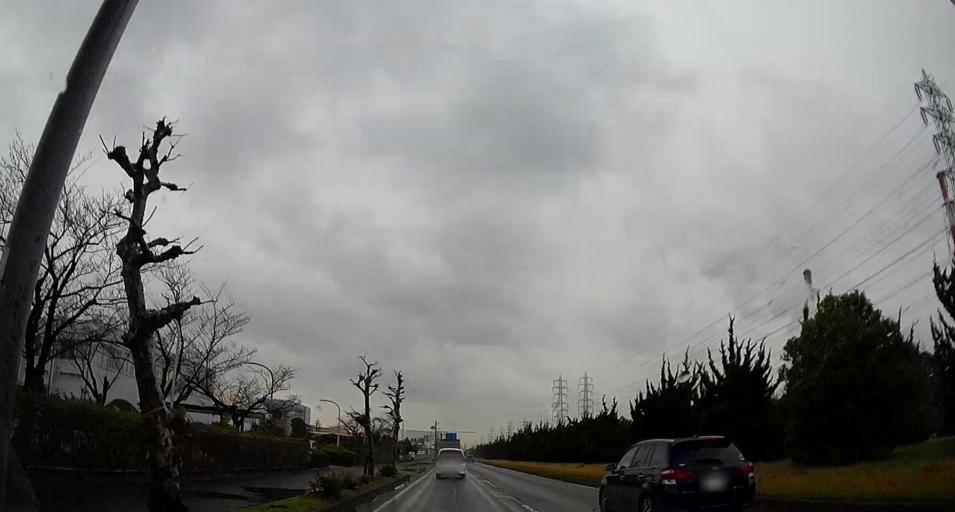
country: JP
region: Chiba
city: Ichihara
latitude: 35.4864
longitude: 140.0403
